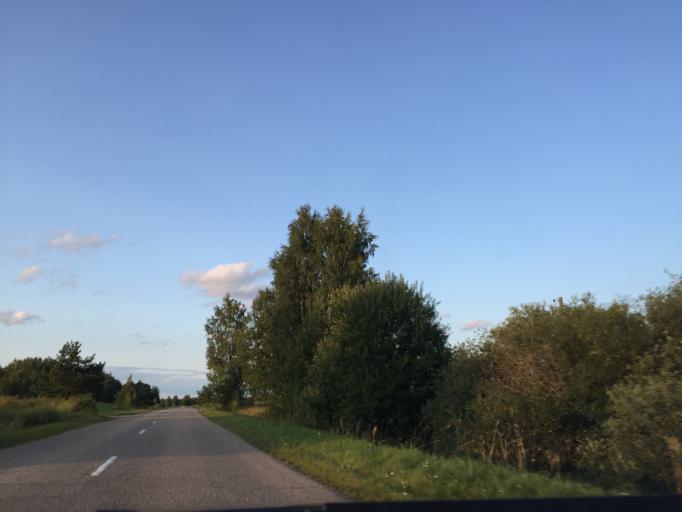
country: LV
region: Dagda
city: Dagda
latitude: 56.2995
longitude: 27.5083
